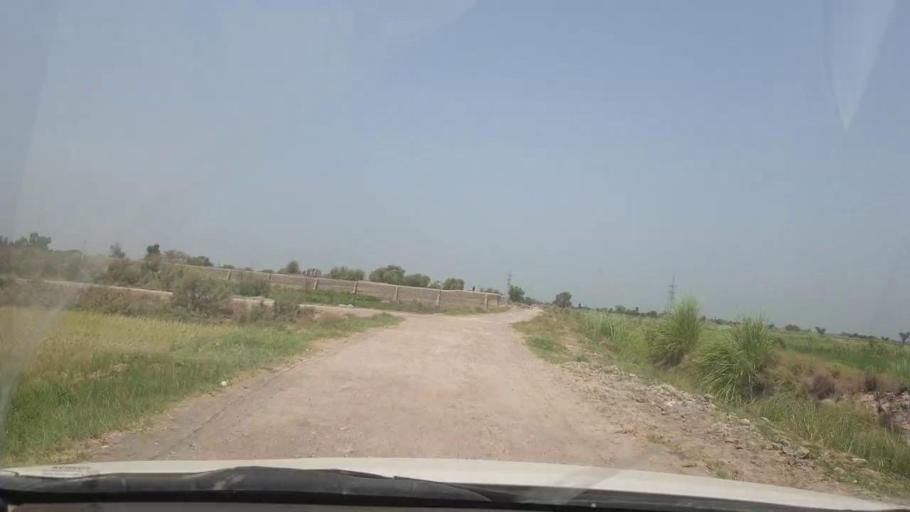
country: PK
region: Sindh
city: Lakhi
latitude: 27.8714
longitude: 68.6941
